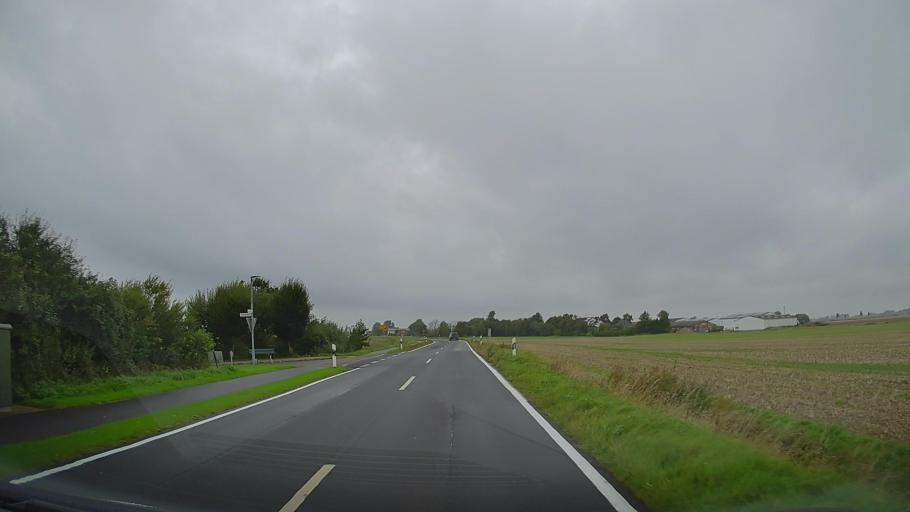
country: DE
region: Schleswig-Holstein
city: Wesselburener Deichhausen
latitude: 54.1428
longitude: 8.9234
